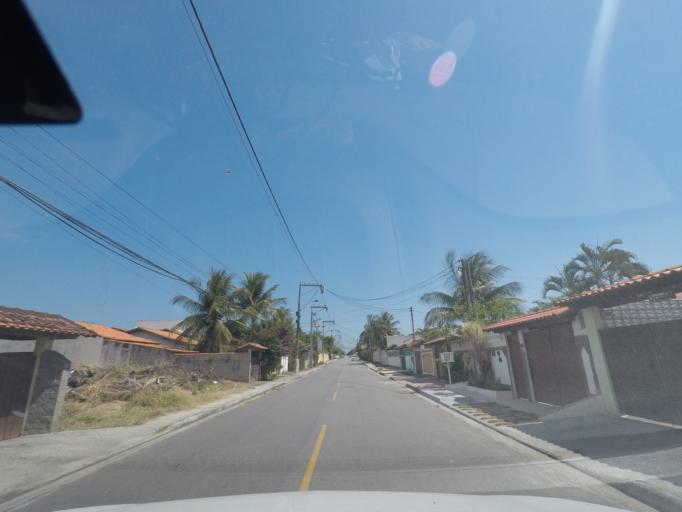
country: BR
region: Rio de Janeiro
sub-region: Marica
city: Marica
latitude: -22.9627
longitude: -42.9631
